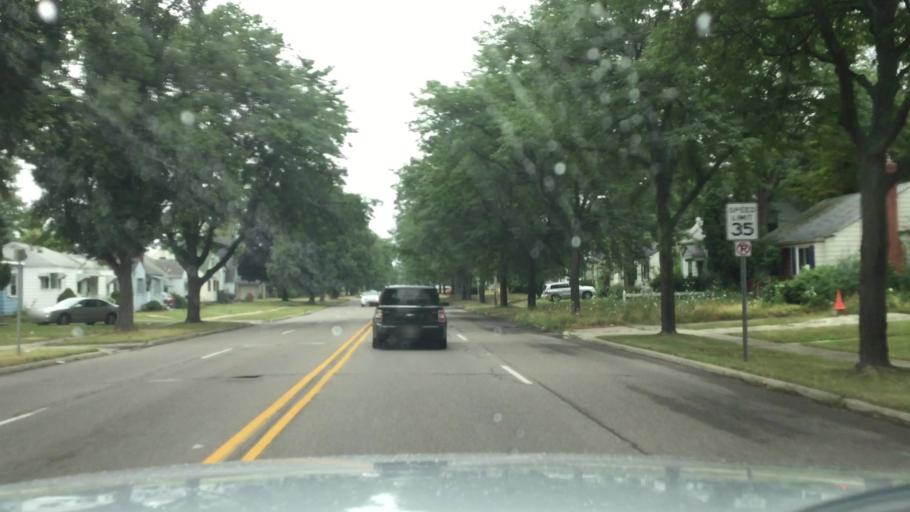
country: US
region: Michigan
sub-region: Genesee County
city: Flint
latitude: 43.0103
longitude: -83.7307
